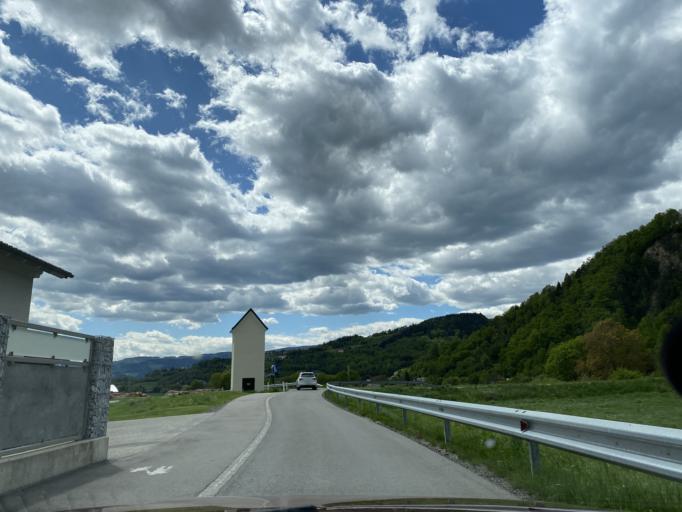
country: AT
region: Carinthia
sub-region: Politischer Bezirk Wolfsberg
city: Wolfsberg
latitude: 46.8595
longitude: 14.8528
